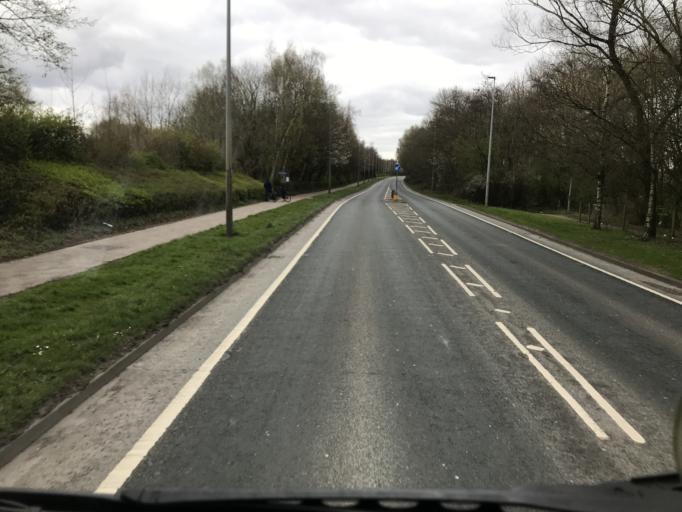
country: GB
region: England
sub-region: City and Borough of Salford
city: Irlam
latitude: 53.4454
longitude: -2.4109
